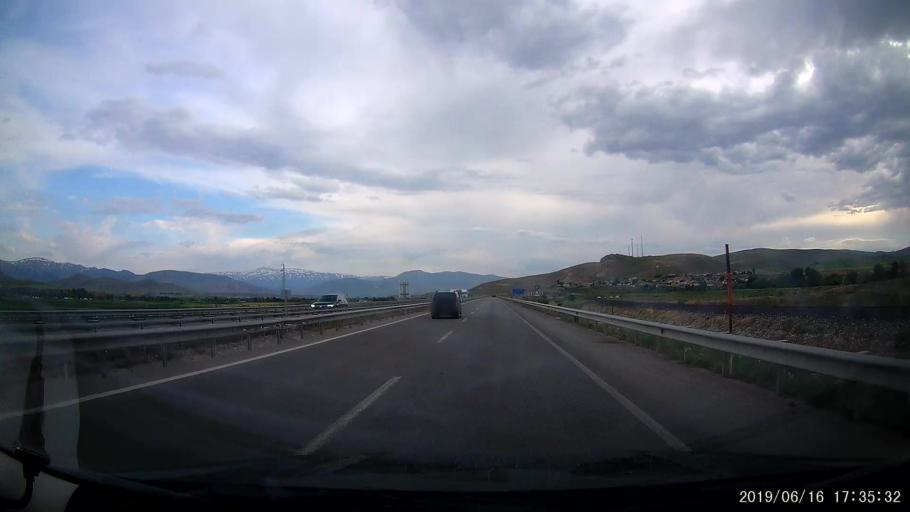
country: TR
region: Erzincan
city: Tercan
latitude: 39.7359
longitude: 40.2620
